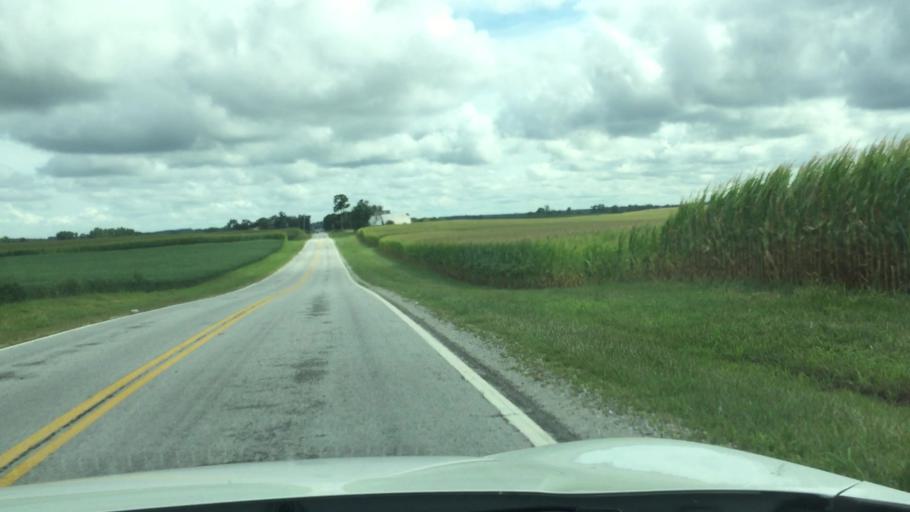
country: US
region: Ohio
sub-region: Clark County
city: Northridge
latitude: 39.9650
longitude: -83.6791
